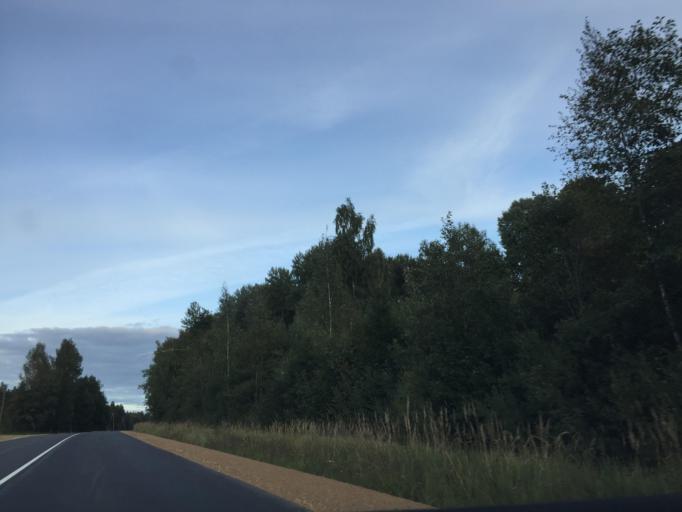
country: LV
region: Salas
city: Sala
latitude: 56.3961
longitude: 25.6992
